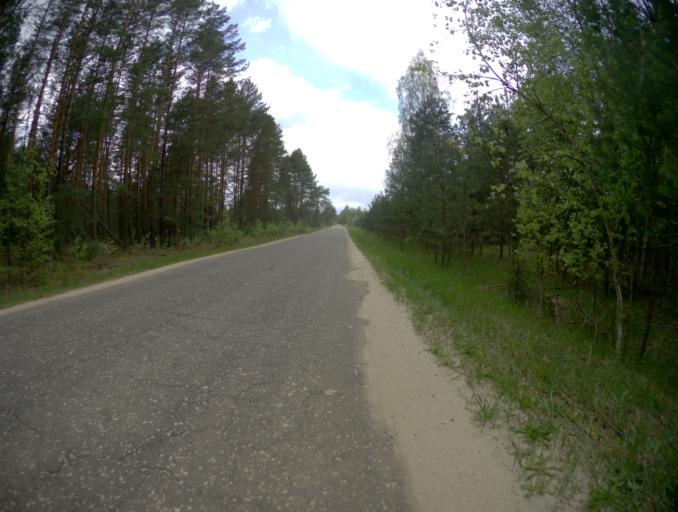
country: RU
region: Vladimir
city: Velikodvorskiy
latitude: 55.2464
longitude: 40.6973
